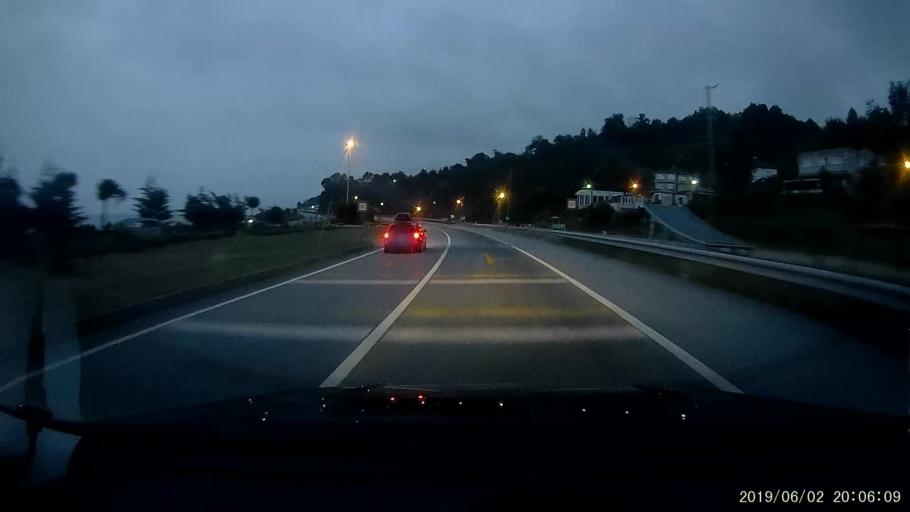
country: TR
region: Giresun
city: Gorele
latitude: 41.0364
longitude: 38.9478
